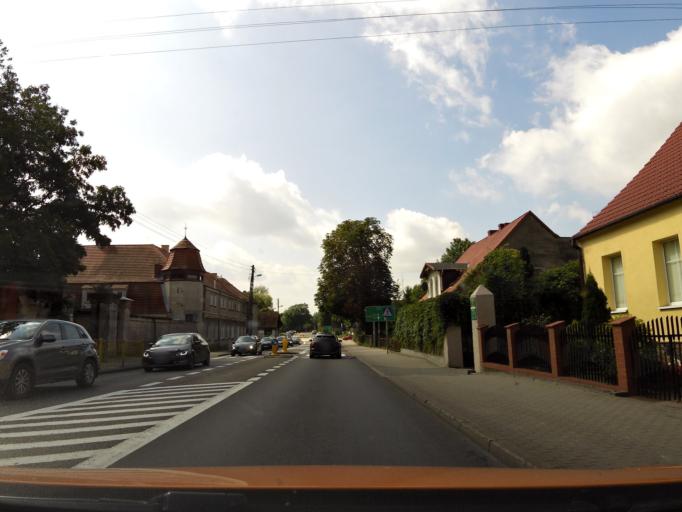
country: PL
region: West Pomeranian Voivodeship
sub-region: Powiat gryficki
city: Ploty
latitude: 53.8034
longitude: 15.2691
